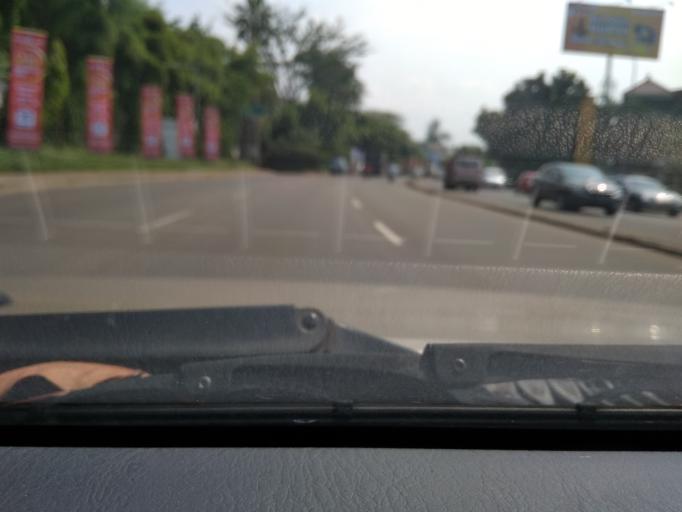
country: ID
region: West Java
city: Serpong
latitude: -6.2703
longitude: 106.6548
